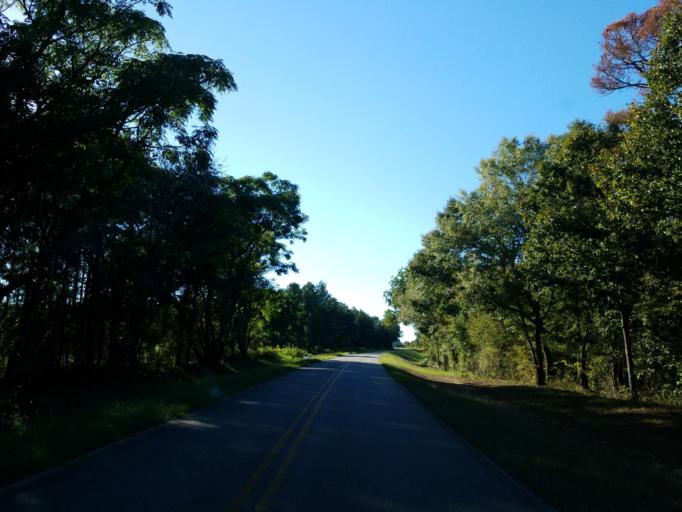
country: US
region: Georgia
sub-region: Lee County
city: Leesburg
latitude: 31.9118
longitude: -84.0282
